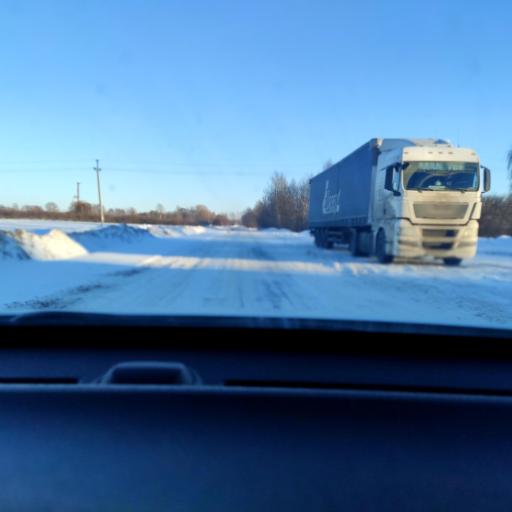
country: RU
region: Tatarstan
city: Stolbishchi
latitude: 55.6440
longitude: 49.2843
